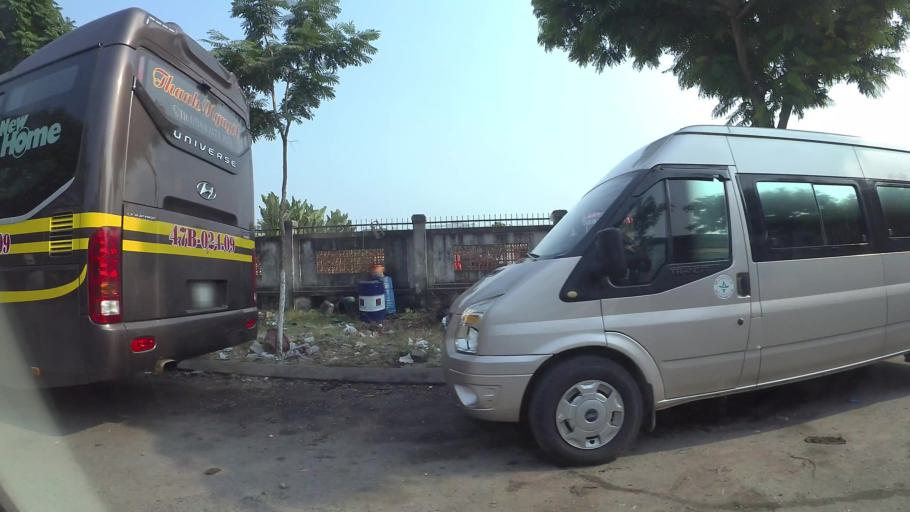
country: VN
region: Da Nang
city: Thanh Khe
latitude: 16.0534
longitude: 108.1744
